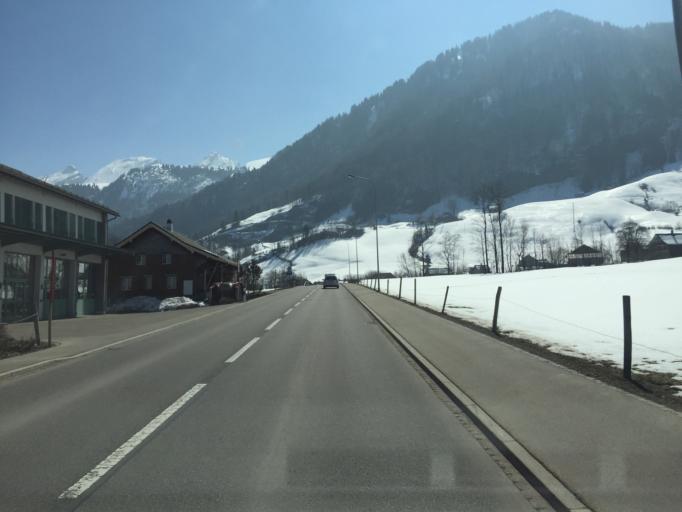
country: CH
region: Saint Gallen
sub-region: Wahlkreis Toggenburg
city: Krummenau
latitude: 47.1970
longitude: 9.2283
